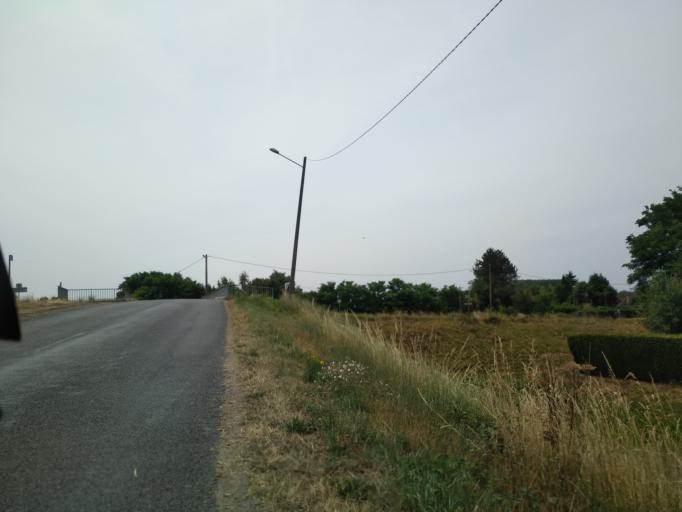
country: FR
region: Bourgogne
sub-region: Departement de Saone-et-Loire
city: Digoin
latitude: 46.4726
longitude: 3.9656
